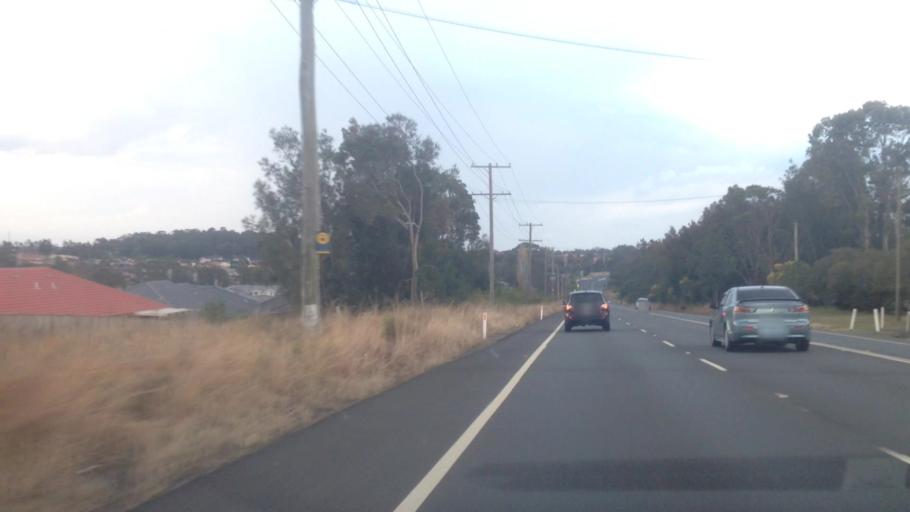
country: AU
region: New South Wales
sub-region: Wyong Shire
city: Kanwal
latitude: -33.2583
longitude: 151.4855
